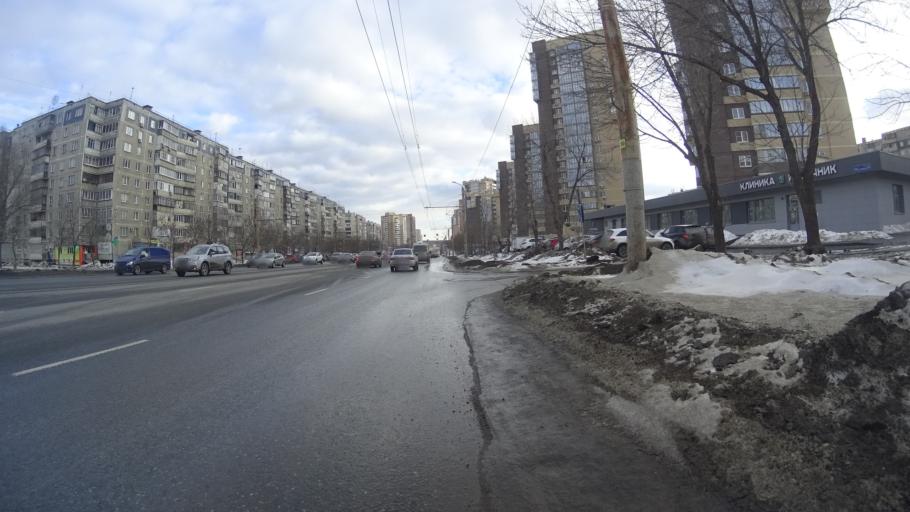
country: RU
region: Chelyabinsk
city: Roshchino
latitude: 55.1799
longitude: 61.2956
